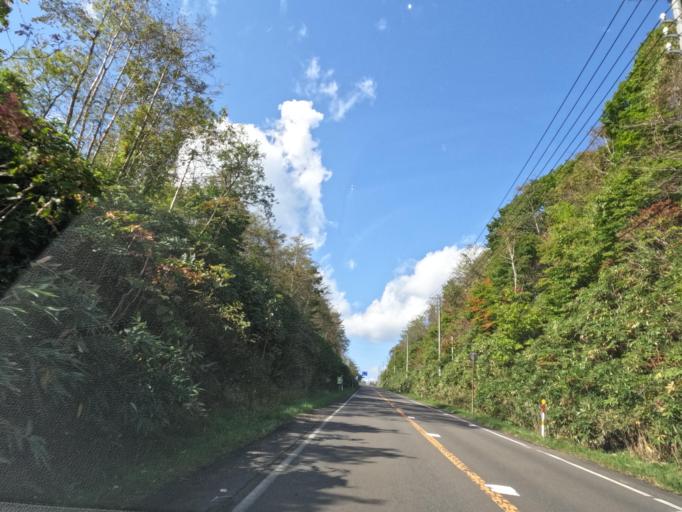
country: JP
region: Hokkaido
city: Muroran
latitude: 42.4759
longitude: 141.1406
